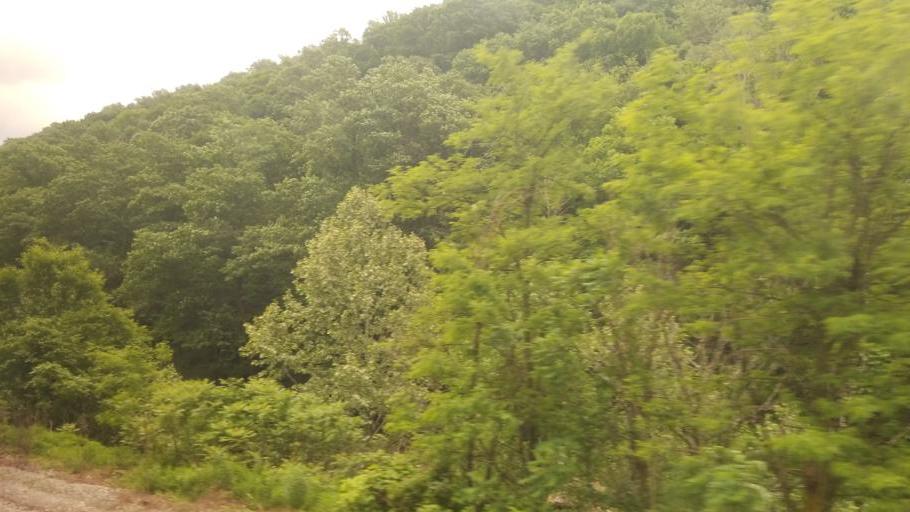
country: US
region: Maryland
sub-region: Allegany County
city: La Vale
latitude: 39.8380
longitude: -78.7853
